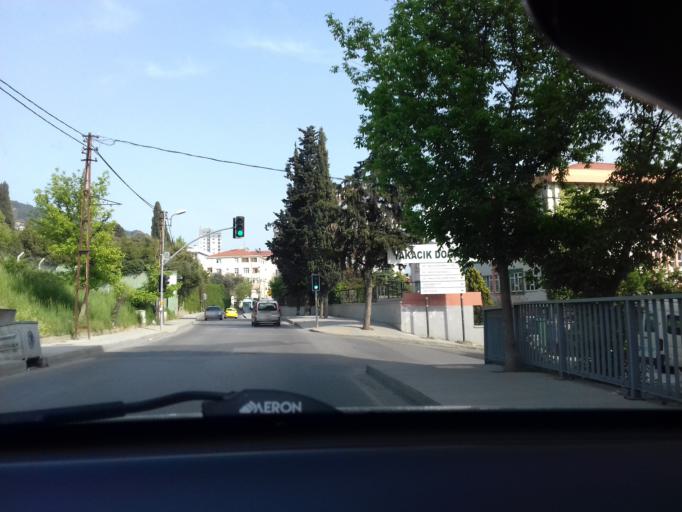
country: TR
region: Istanbul
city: Pendik
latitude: 40.9136
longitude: 29.2258
